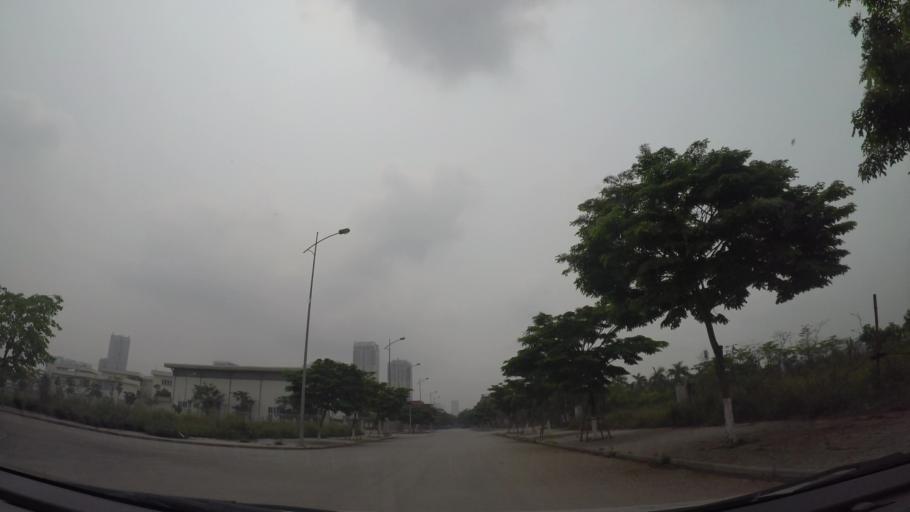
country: VN
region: Ha Noi
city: Ha Dong
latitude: 20.9768
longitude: 105.7512
